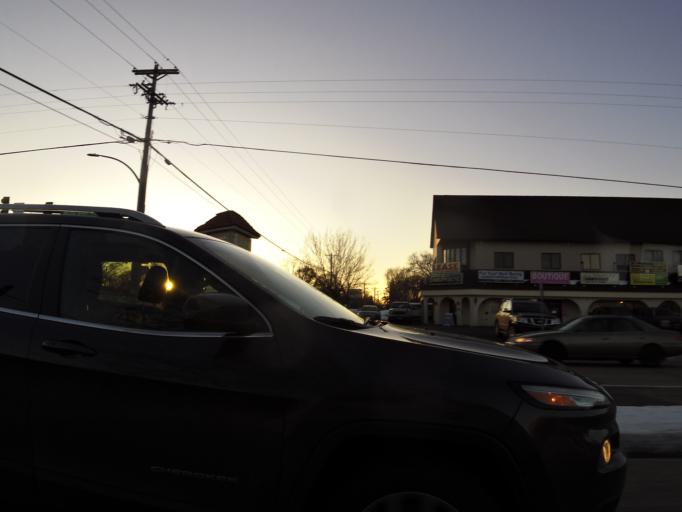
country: US
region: Minnesota
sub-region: Ramsey County
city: White Bear Lake
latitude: 45.0504
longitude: -93.0153
